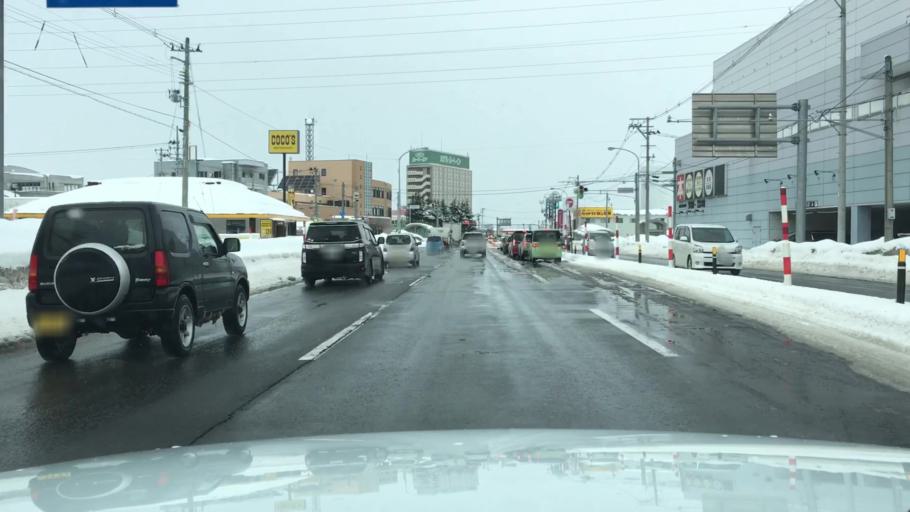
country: JP
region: Aomori
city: Hirosaki
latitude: 40.6003
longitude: 140.5010
